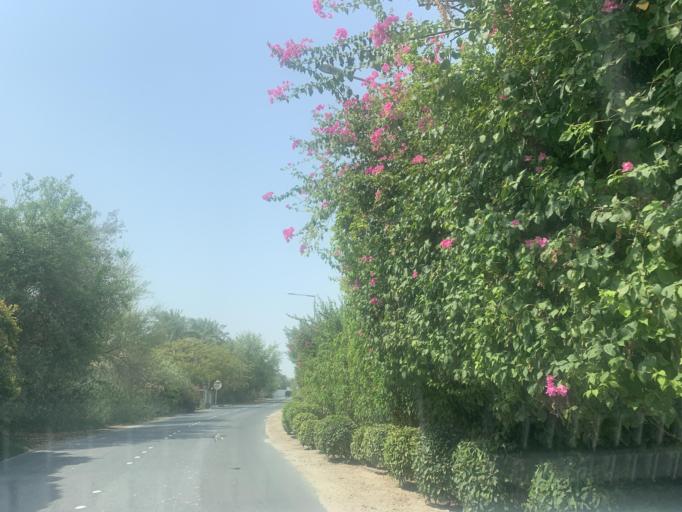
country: BH
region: Central Governorate
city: Madinat Hamad
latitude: 26.1677
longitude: 50.4534
